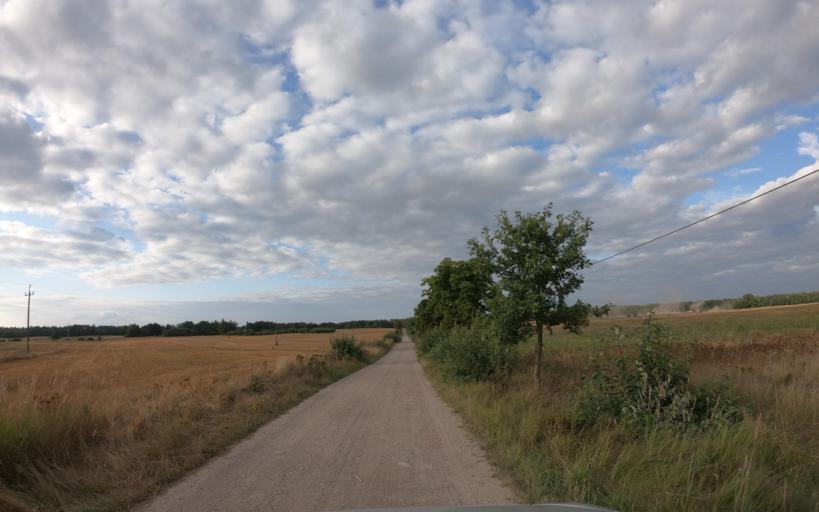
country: PL
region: West Pomeranian Voivodeship
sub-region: Powiat drawski
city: Czaplinek
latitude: 53.5272
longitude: 16.1536
